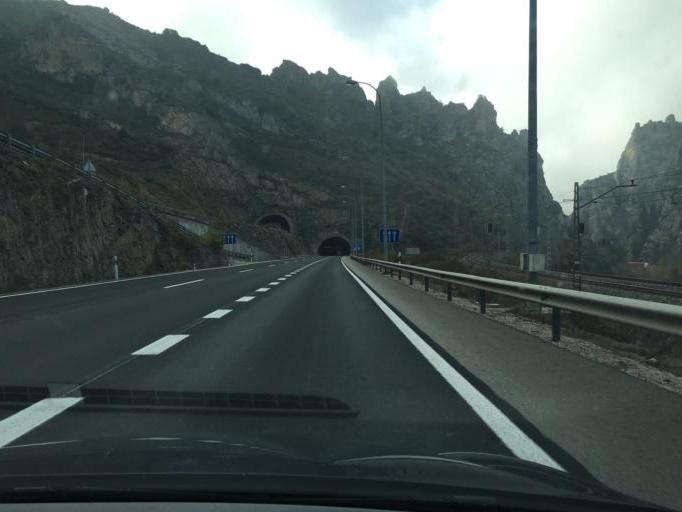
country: ES
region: Castille and Leon
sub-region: Provincia de Burgos
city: Pancorbo
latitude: 42.6426
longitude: -3.0942
